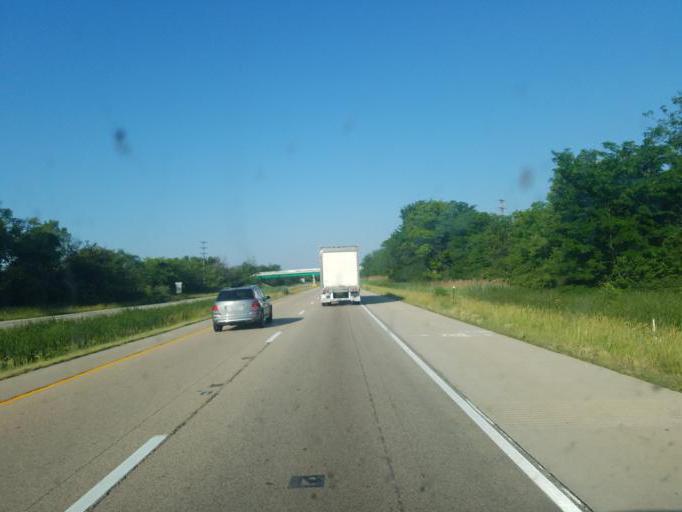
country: US
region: Illinois
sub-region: Grundy County
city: Morris
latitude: 41.3844
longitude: -88.4308
